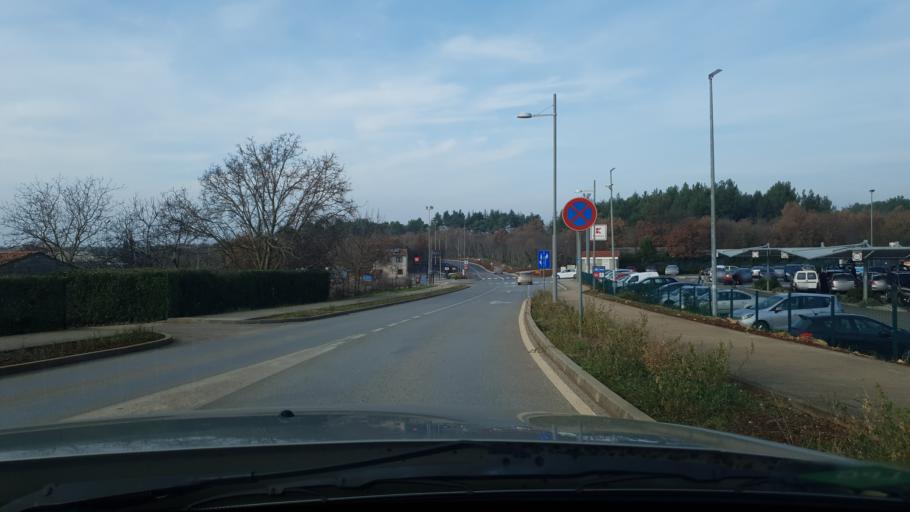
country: HR
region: Istarska
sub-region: Grad Porec
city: Porec
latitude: 45.2310
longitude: 13.6208
